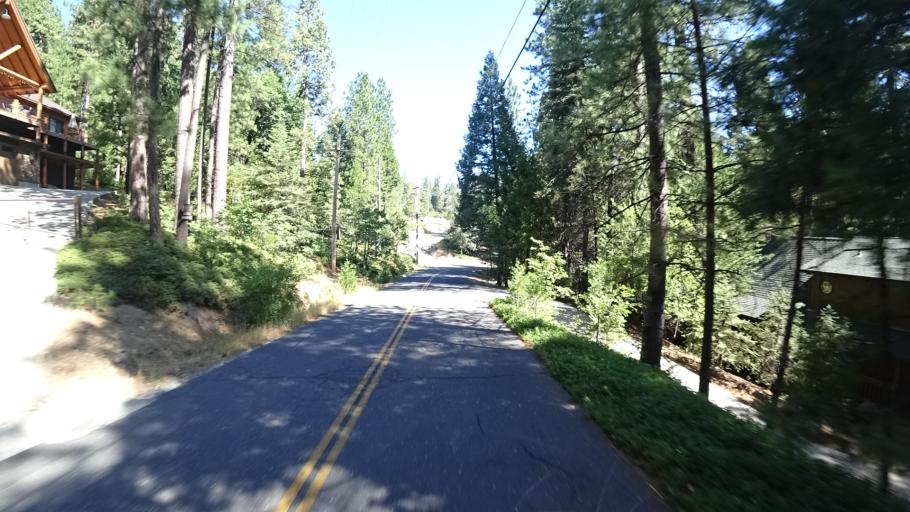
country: US
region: California
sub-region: Calaveras County
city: Arnold
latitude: 38.2460
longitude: -120.3656
